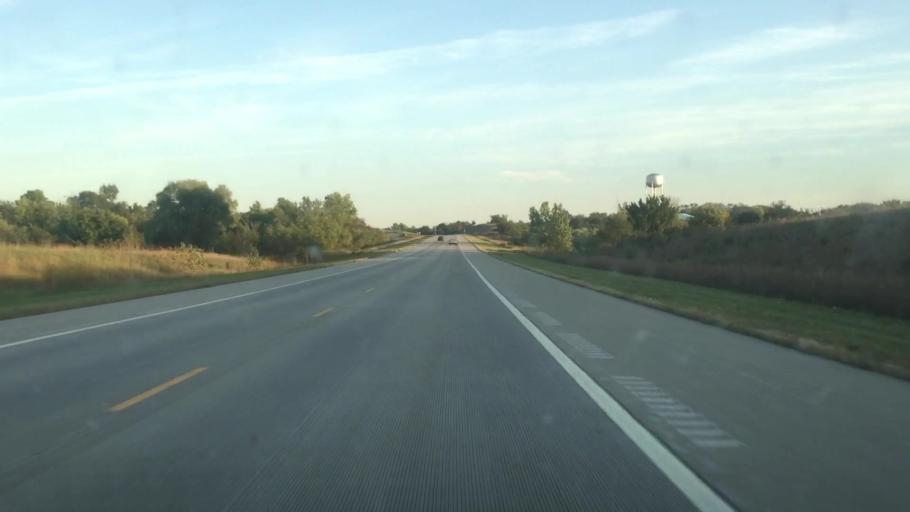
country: US
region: Kansas
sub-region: Leavenworth County
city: Leavenworth
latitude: 39.3752
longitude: -95.0551
